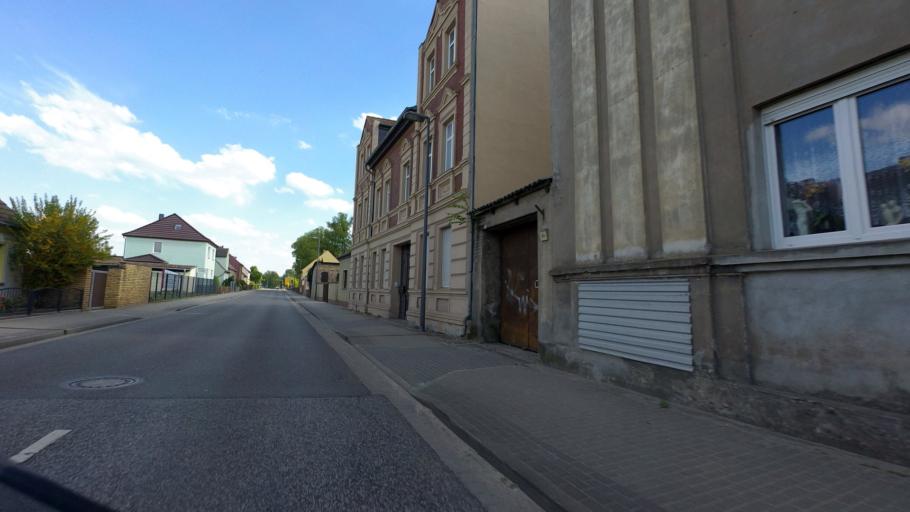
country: DE
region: Brandenburg
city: Zehdenick
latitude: 52.9834
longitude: 13.3435
